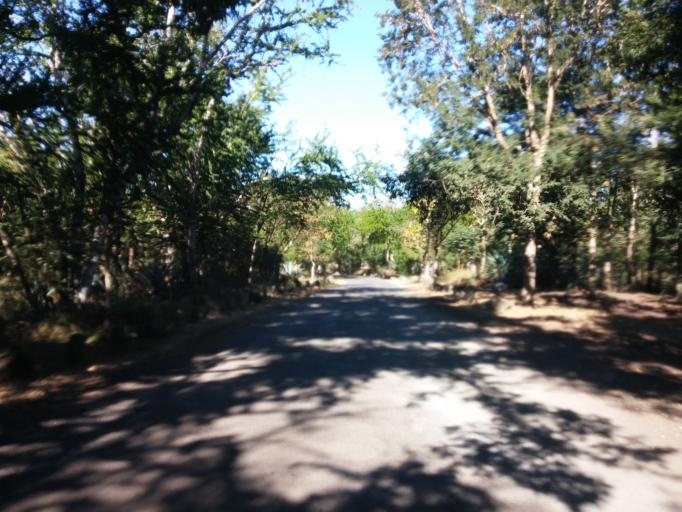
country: RE
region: Reunion
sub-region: Reunion
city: Les Avirons
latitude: -21.2647
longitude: 55.3537
